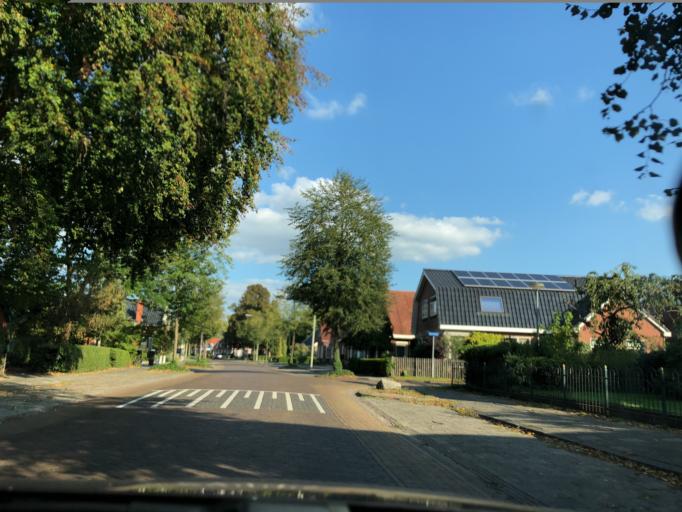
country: NL
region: Groningen
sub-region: Gemeente Vlagtwedde
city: Vlagtwedde
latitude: 53.0252
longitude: 7.1151
